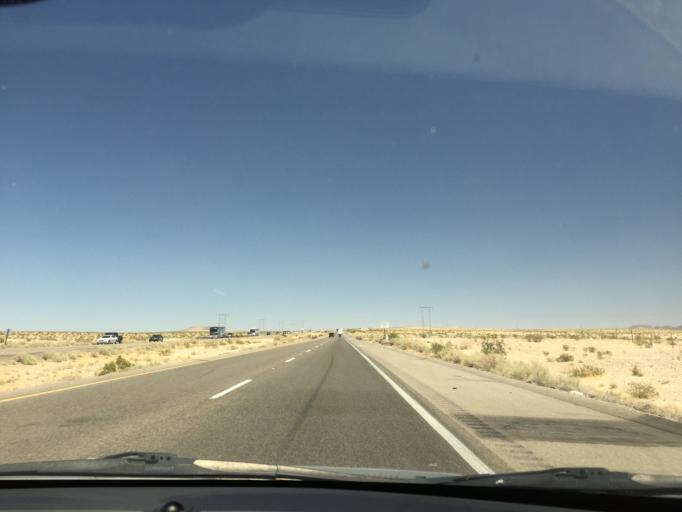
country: US
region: California
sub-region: San Bernardino County
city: Fort Irwin
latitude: 35.0041
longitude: -116.5501
